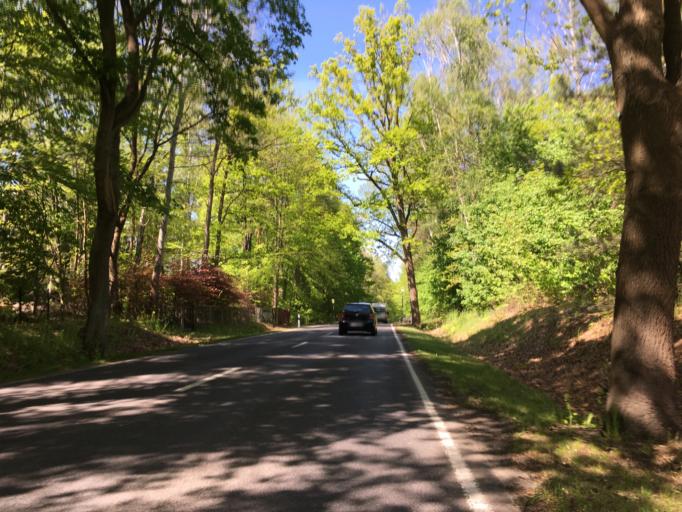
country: DE
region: Brandenburg
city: Marienwerder
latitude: 52.7839
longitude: 13.5563
